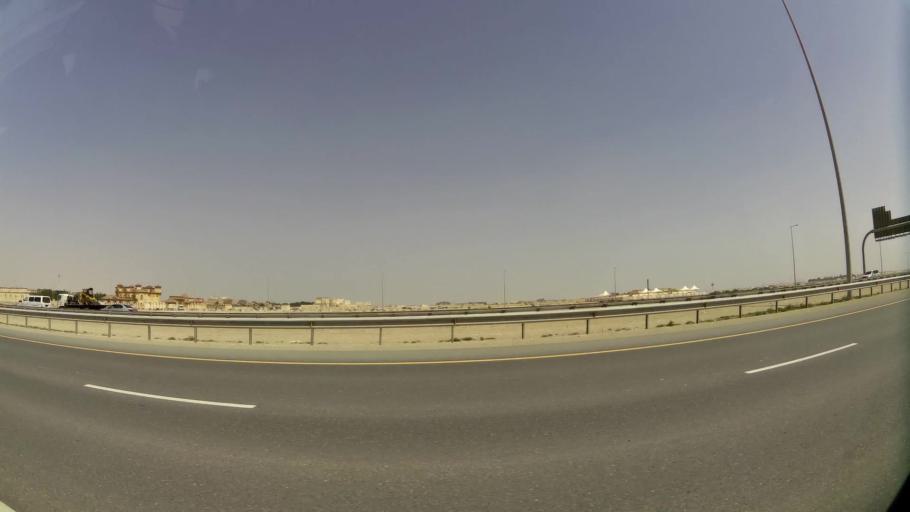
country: QA
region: Baladiyat Umm Salal
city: Umm Salal Muhammad
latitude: 25.4303
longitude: 51.4147
